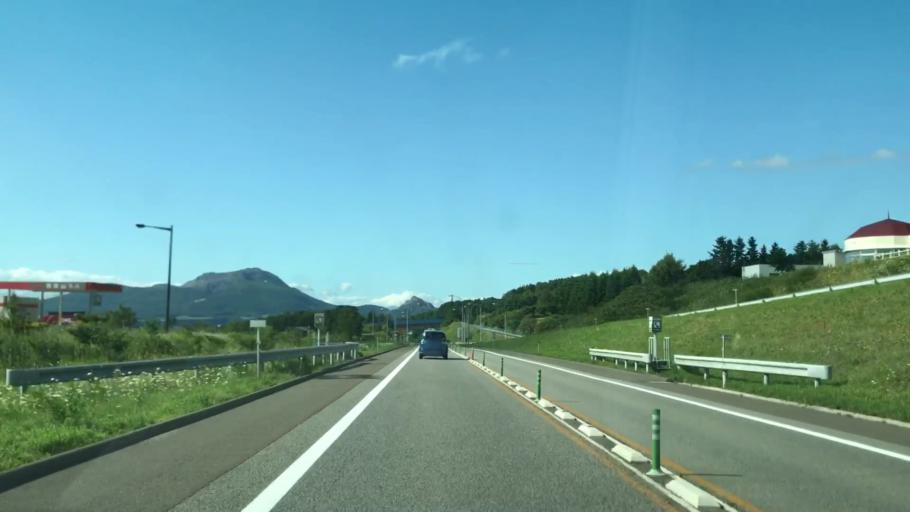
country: JP
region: Hokkaido
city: Date
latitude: 42.4660
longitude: 140.9088
